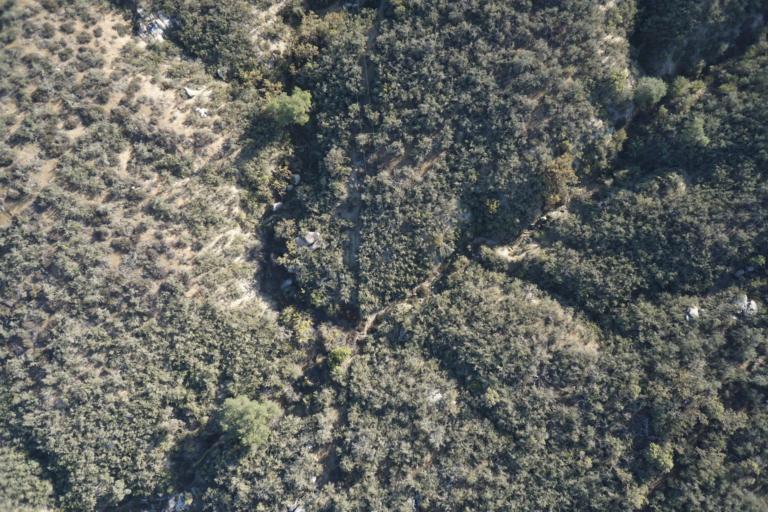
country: US
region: California
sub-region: Riverside County
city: East Hemet
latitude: 33.6142
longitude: -116.9140
